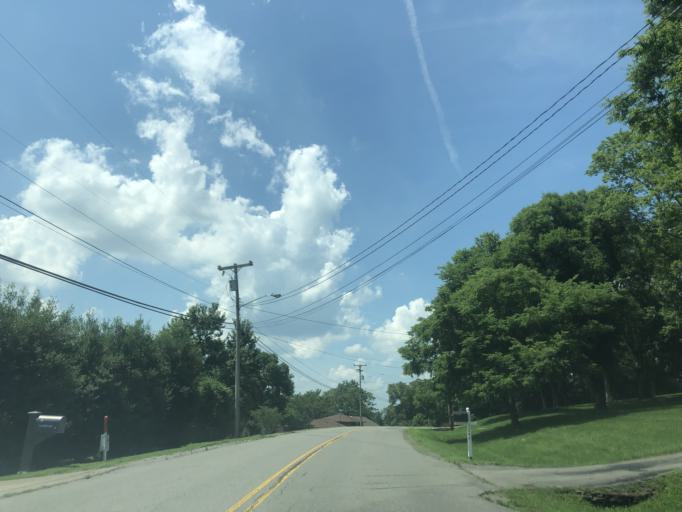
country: US
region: Tennessee
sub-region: Davidson County
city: Lakewood
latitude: 36.1730
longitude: -86.6717
